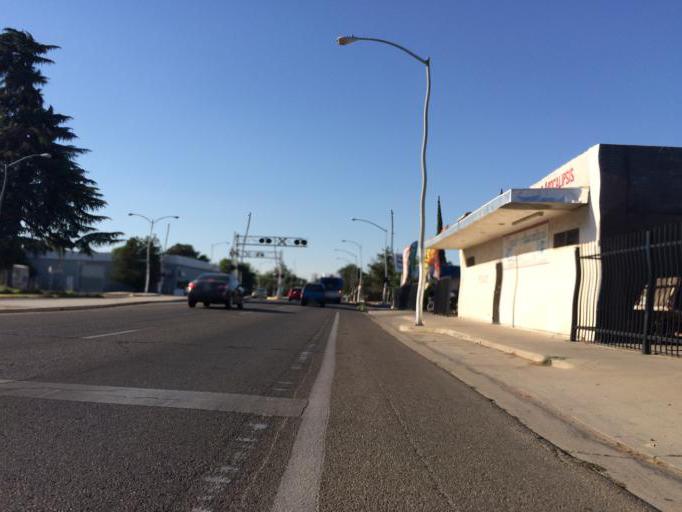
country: US
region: California
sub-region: Fresno County
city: Fresno
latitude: 36.7606
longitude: -119.7724
